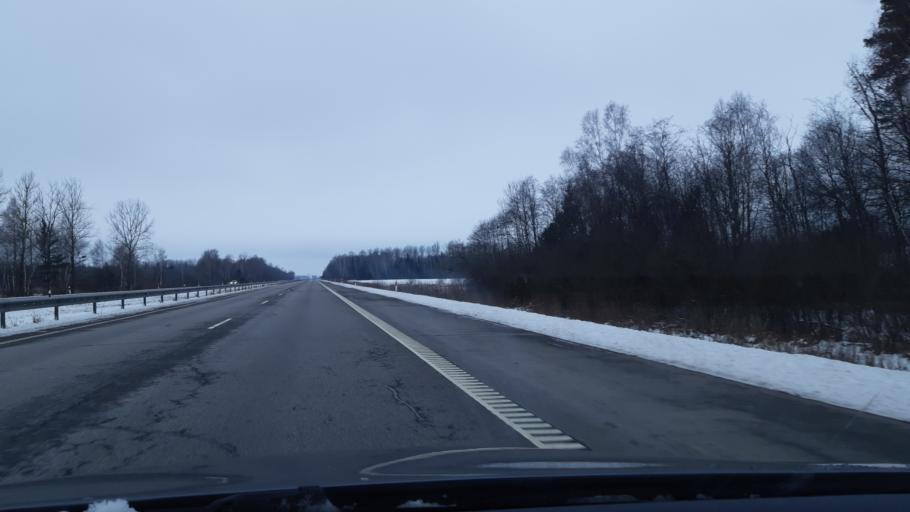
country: LT
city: Vilkija
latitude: 55.1266
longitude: 23.7461
